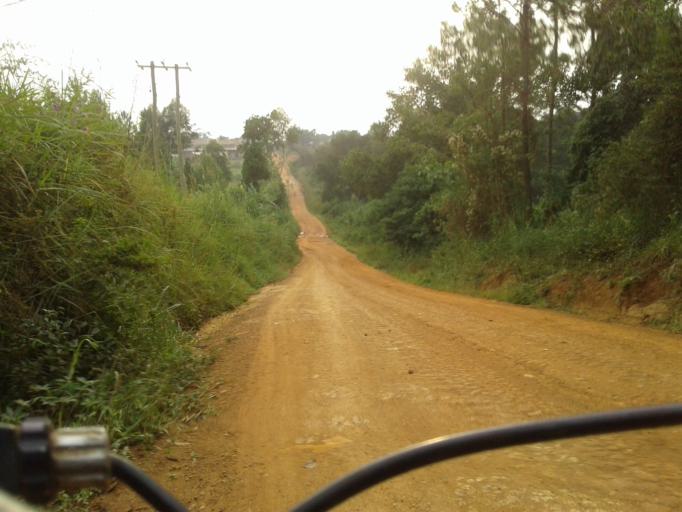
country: UG
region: Western Region
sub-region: Hoima District
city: Hoima
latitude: 1.4255
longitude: 31.3264
